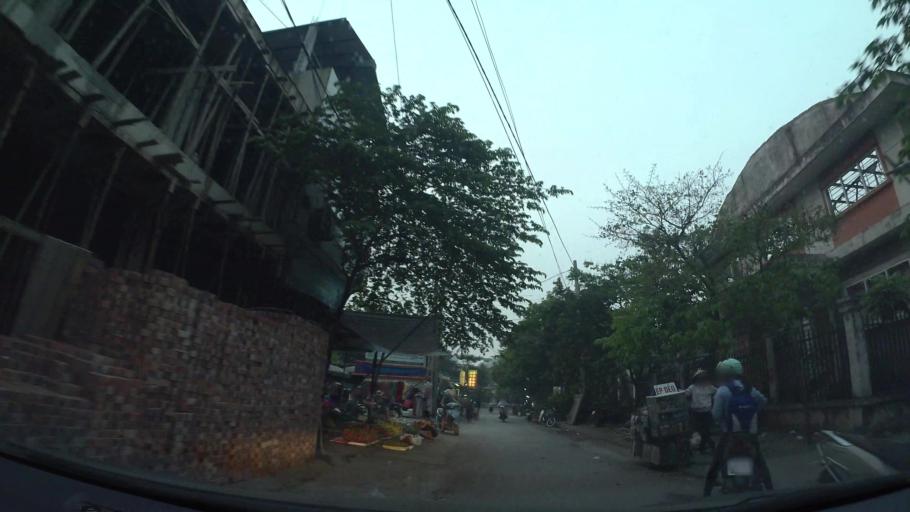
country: VN
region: Ha Noi
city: Ha Dong
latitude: 20.9691
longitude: 105.7868
